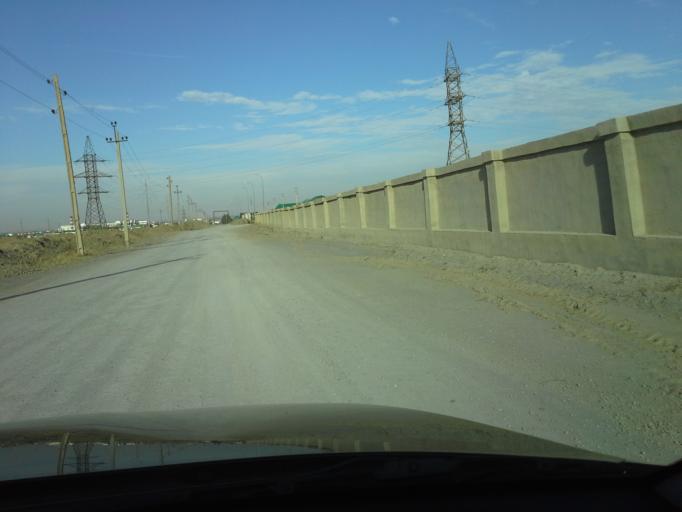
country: TM
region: Ahal
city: Abadan
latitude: 38.0416
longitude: 58.1625
